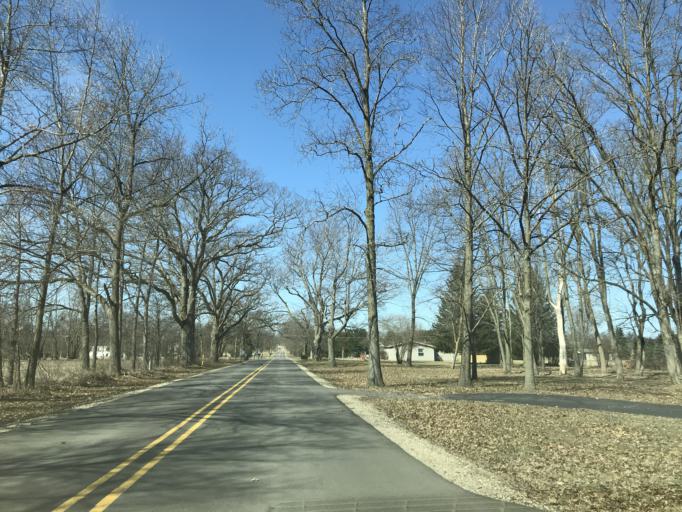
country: US
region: Michigan
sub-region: Hillsdale County
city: Jonesville
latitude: 41.9855
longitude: -84.6738
